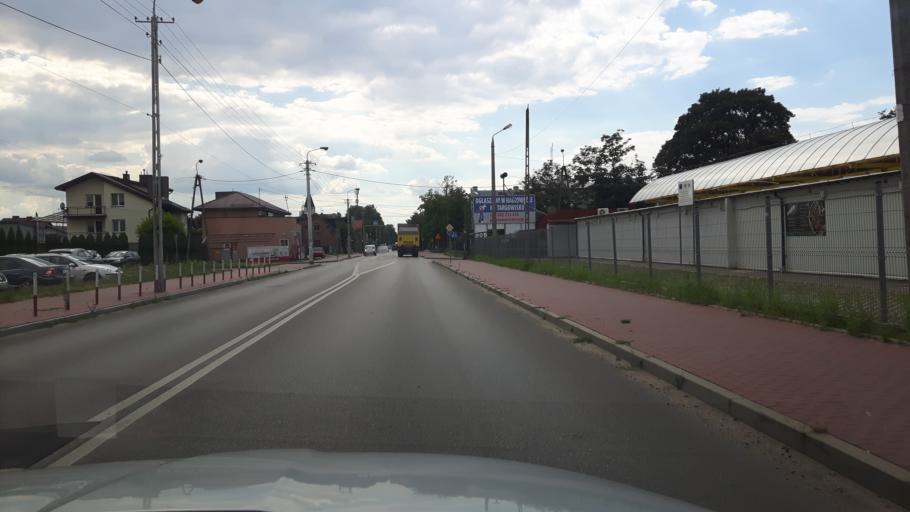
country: PL
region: Masovian Voivodeship
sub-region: Powiat wolominski
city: Wolomin
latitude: 52.3393
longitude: 21.2467
